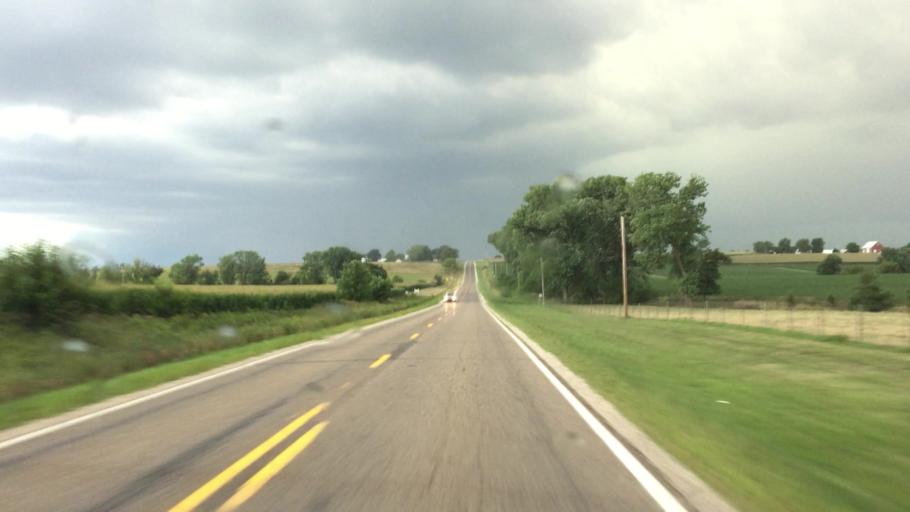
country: US
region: Iowa
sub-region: Henry County
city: Mount Pleasant
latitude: 40.7844
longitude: -91.5370
